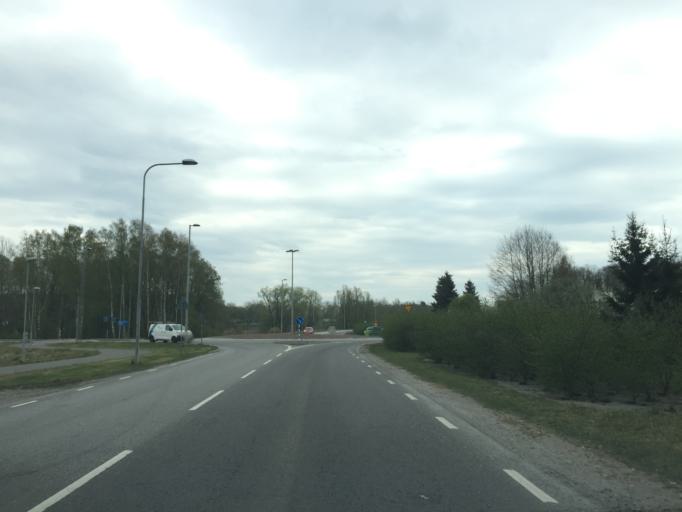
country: SE
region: Vaestra Goetaland
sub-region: Goteborg
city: Loevgaerdet
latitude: 57.8084
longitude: 12.0403
